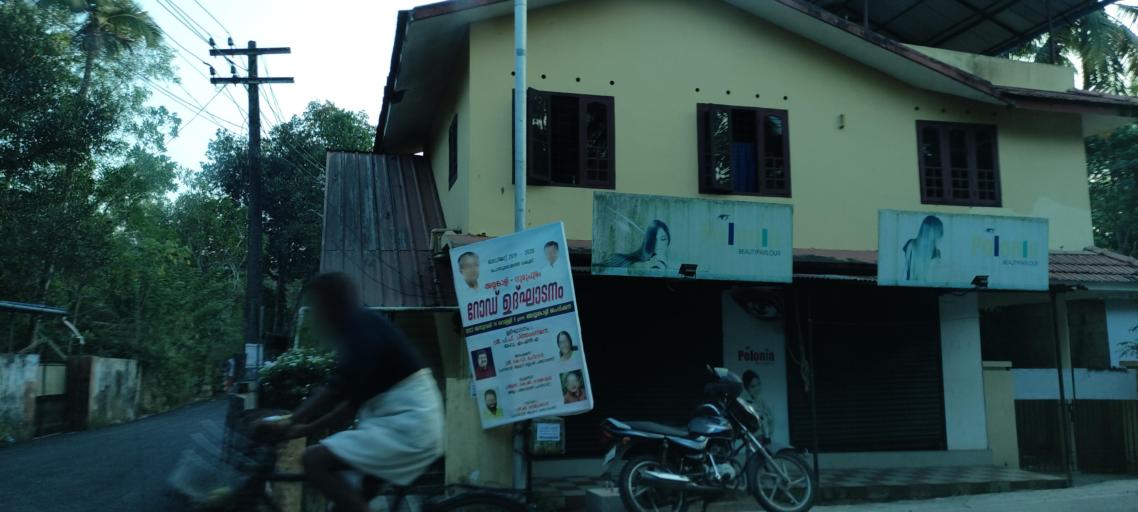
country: IN
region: Kerala
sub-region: Alappuzha
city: Alleppey
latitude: 9.5350
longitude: 76.3340
